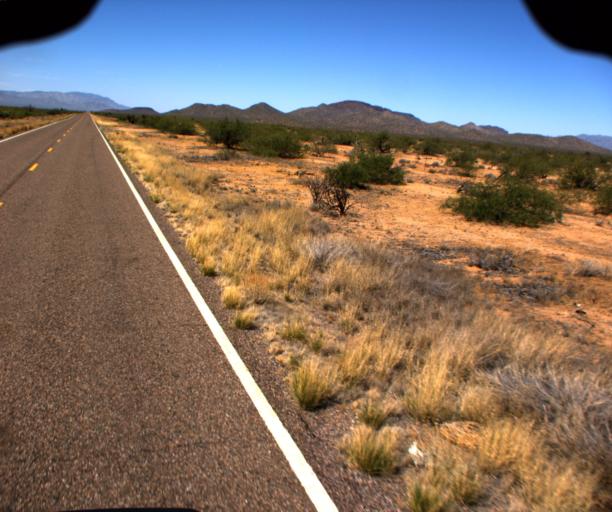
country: US
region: Arizona
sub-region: Yavapai County
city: Congress
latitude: 34.0579
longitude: -113.0491
